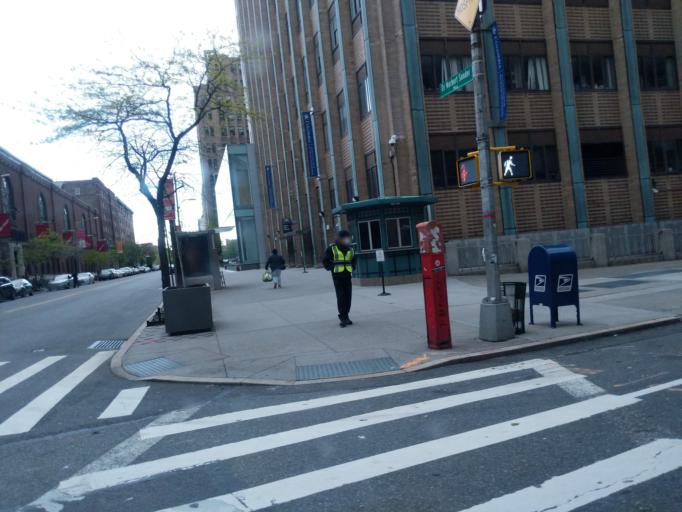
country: US
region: New York
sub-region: New York County
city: Inwood
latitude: 40.8418
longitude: -73.9421
